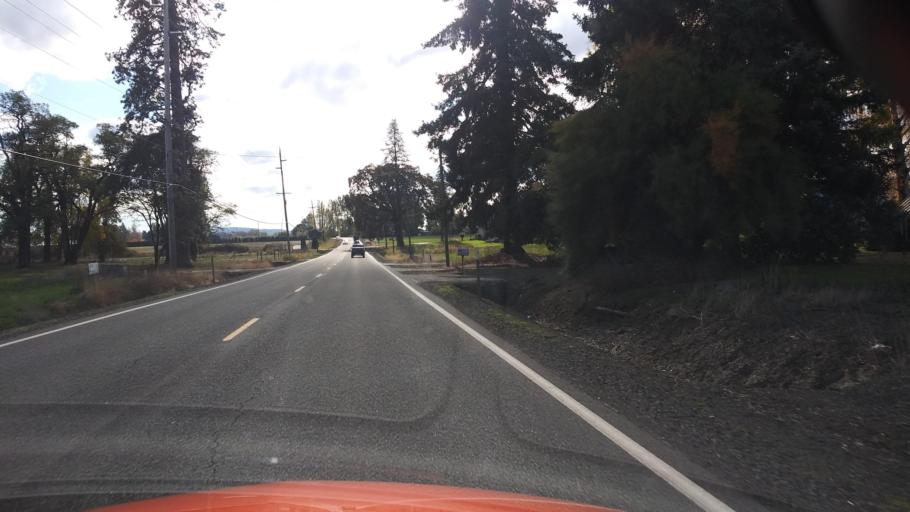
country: US
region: Oregon
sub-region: Washington County
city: Banks
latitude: 45.5874
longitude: -123.1144
